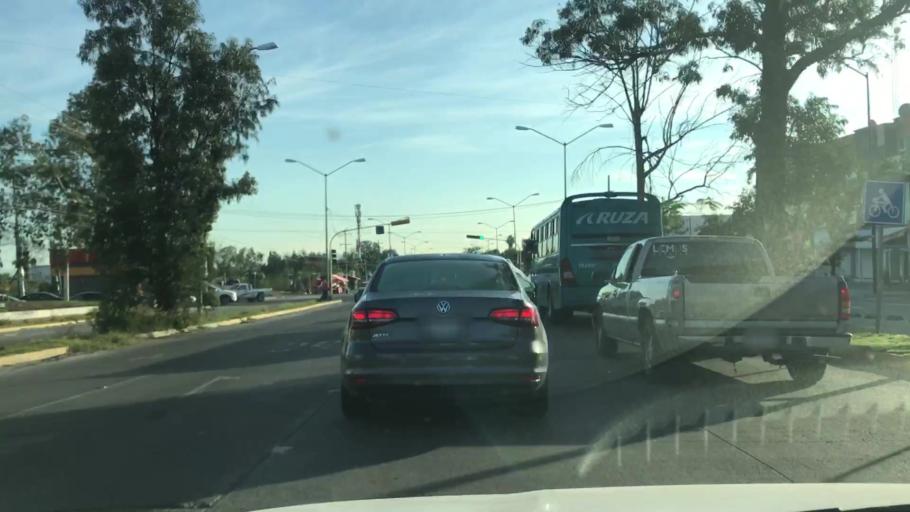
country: MX
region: Jalisco
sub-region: Tlajomulco de Zuniga
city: Palomar
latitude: 20.6251
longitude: -103.4653
